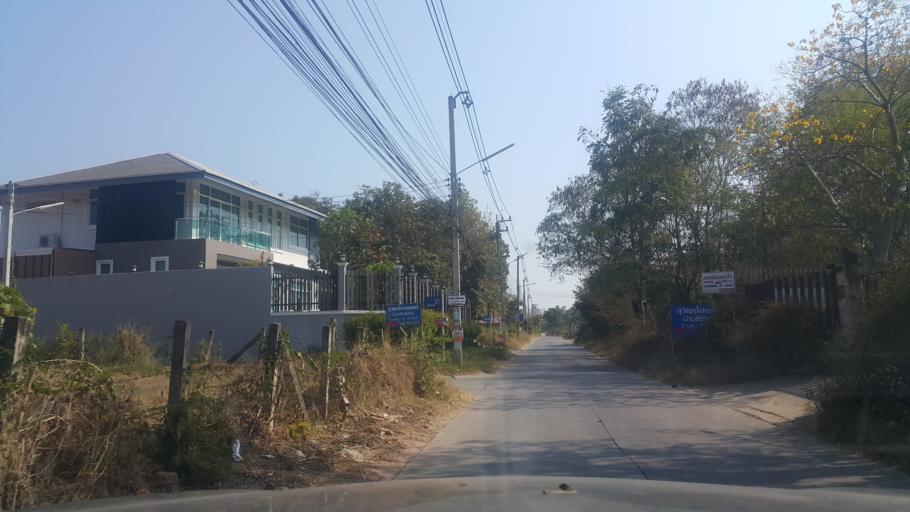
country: TH
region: Nakhon Ratchasima
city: Nakhon Ratchasima
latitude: 14.9328
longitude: 102.0493
